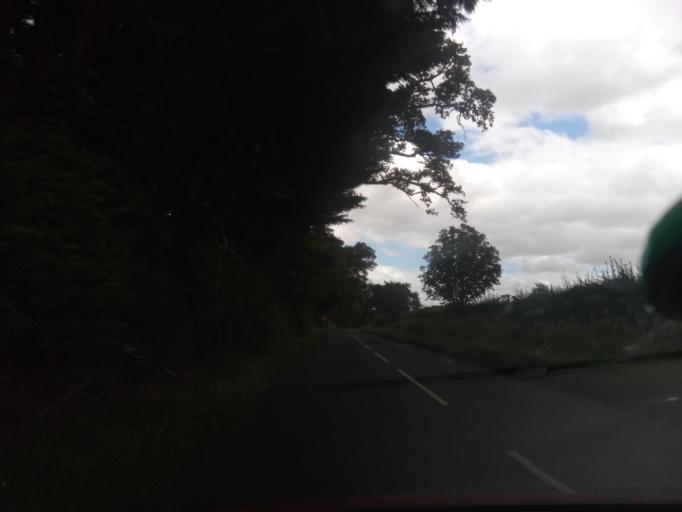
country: GB
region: Scotland
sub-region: The Scottish Borders
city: Kelso
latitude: 55.6021
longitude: -2.4145
